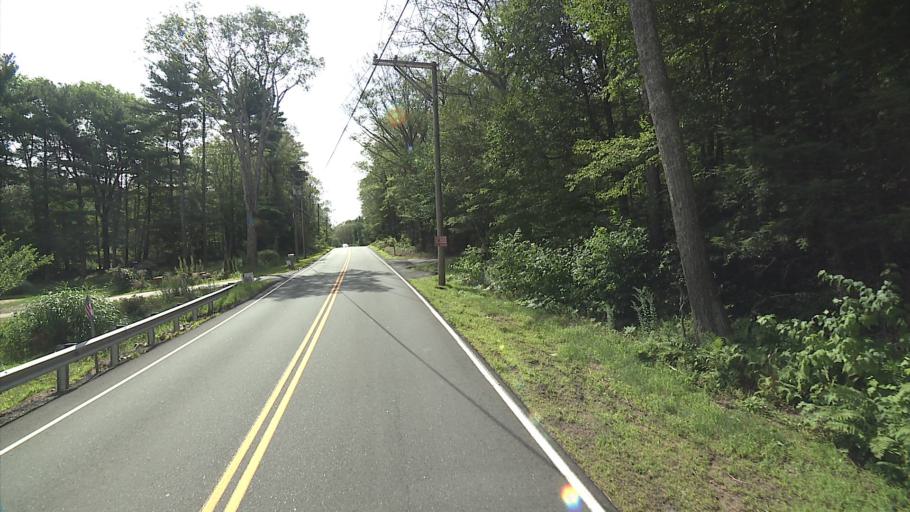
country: US
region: Massachusetts
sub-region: Hampden County
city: Holland
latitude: 41.9872
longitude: -72.1217
